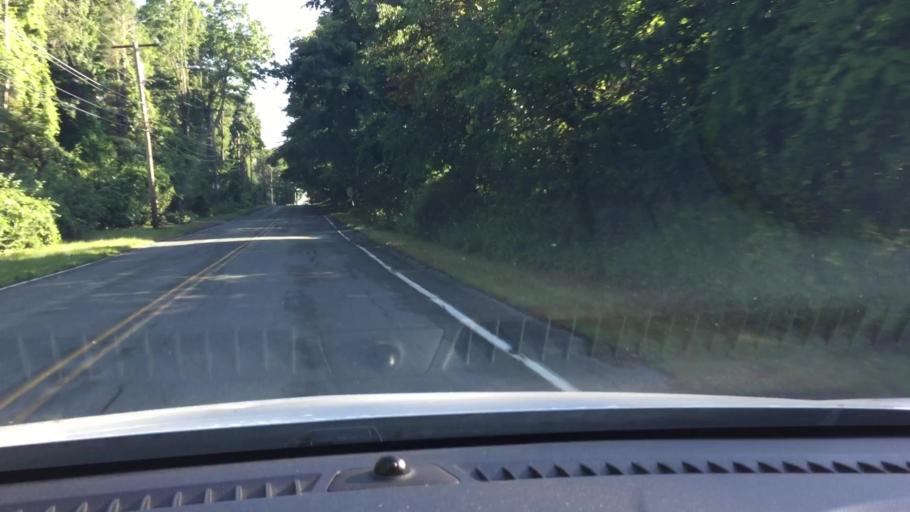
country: US
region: Massachusetts
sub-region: Berkshire County
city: Pittsfield
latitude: 42.4320
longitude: -73.2261
